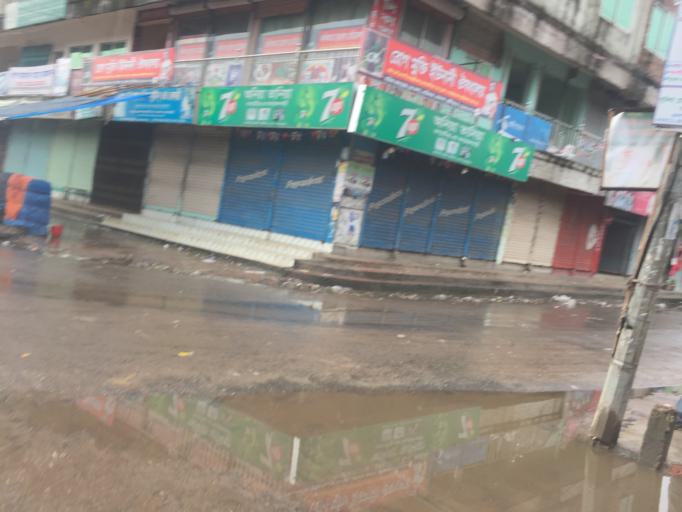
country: BD
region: Dhaka
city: Narayanganj
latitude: 23.5466
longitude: 90.4857
